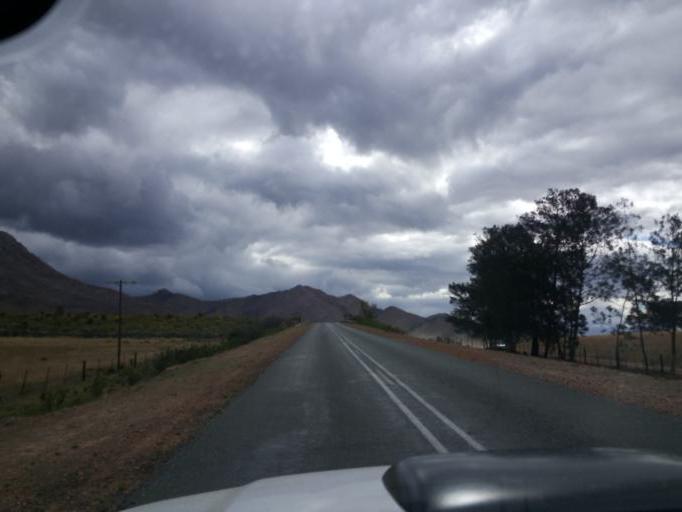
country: ZA
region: Western Cape
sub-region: Eden District Municipality
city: George
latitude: -33.8269
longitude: 22.4075
